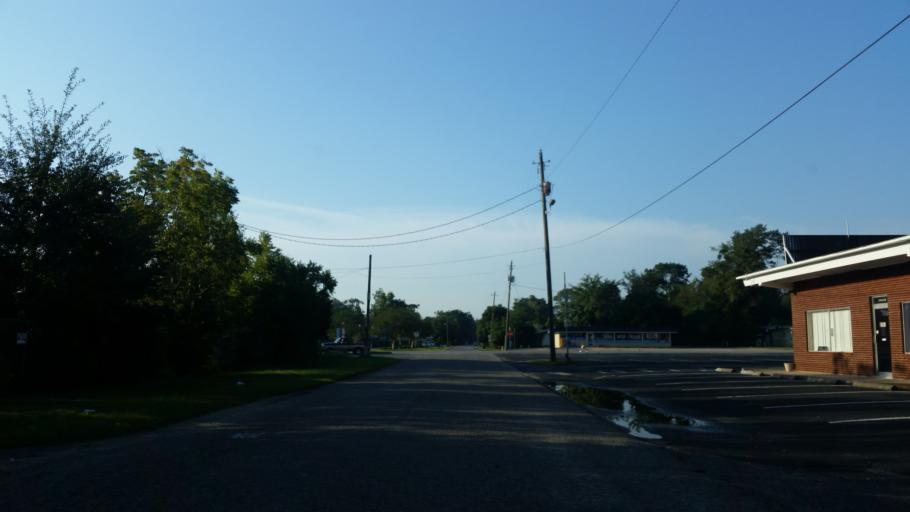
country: US
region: Florida
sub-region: Santa Rosa County
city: Milton
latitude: 30.6225
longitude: -87.0414
